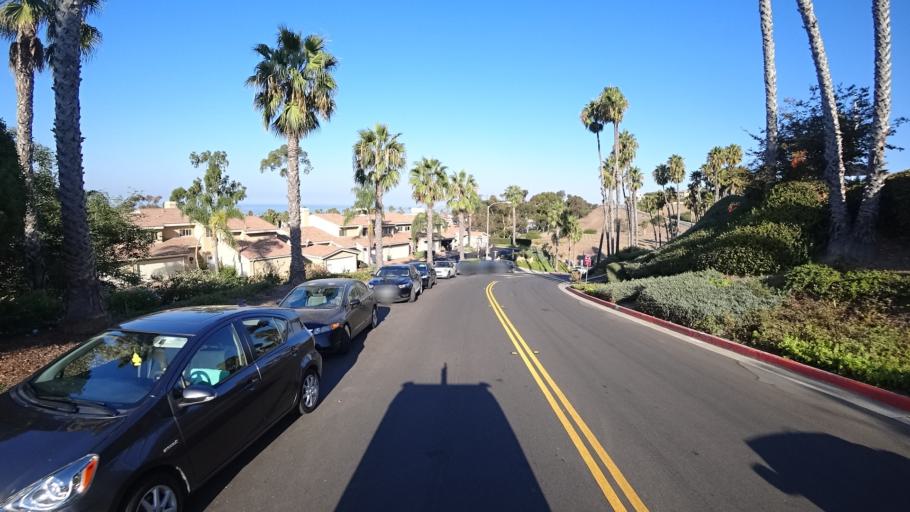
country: US
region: California
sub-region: Orange County
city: San Clemente
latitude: 33.4269
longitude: -117.6089
